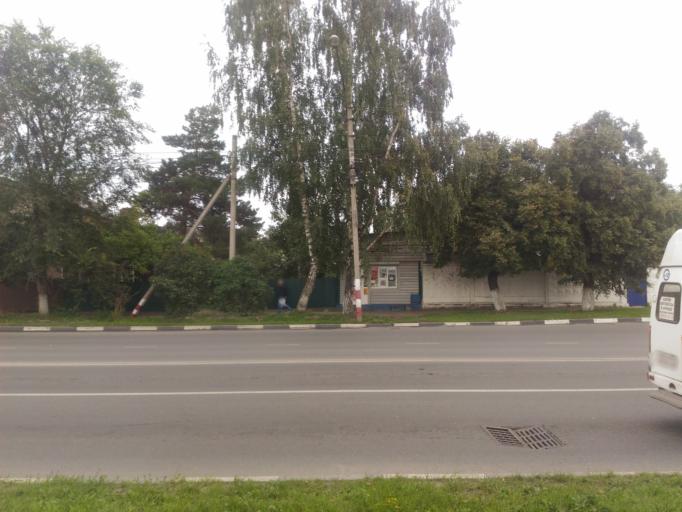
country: RU
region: Ulyanovsk
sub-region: Ulyanovskiy Rayon
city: Ulyanovsk
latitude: 54.2738
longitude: 48.3317
